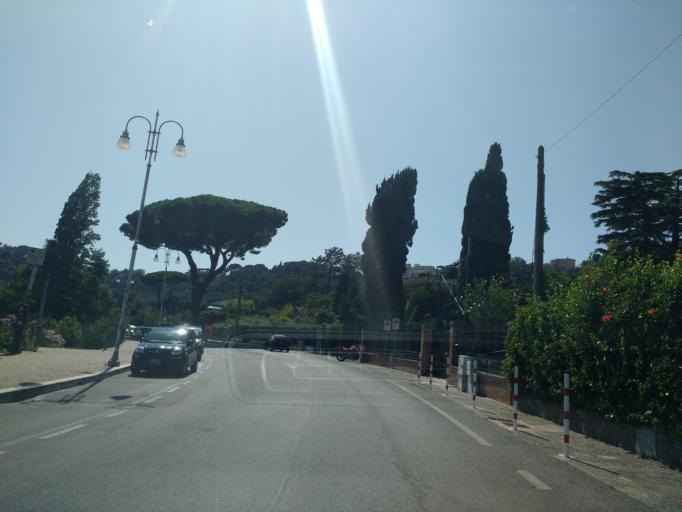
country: IT
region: Latium
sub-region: Citta metropolitana di Roma Capitale
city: Castel Gandolfo
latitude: 41.7616
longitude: 12.6584
